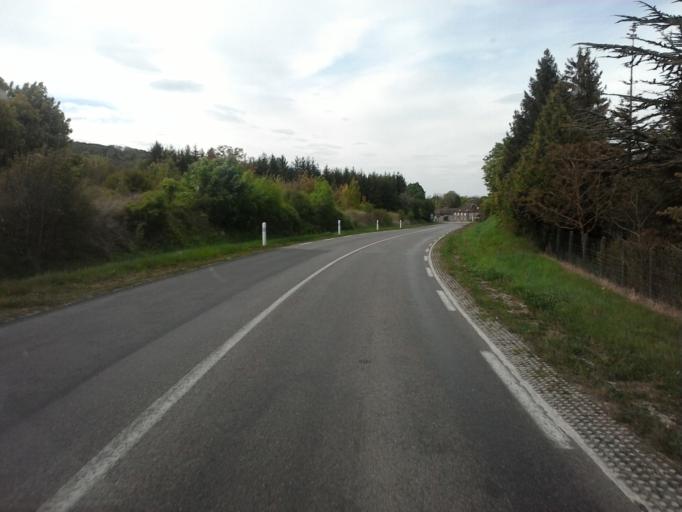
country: FR
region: Champagne-Ardenne
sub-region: Departement de l'Aube
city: Bouilly
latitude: 48.1664
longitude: 4.0216
